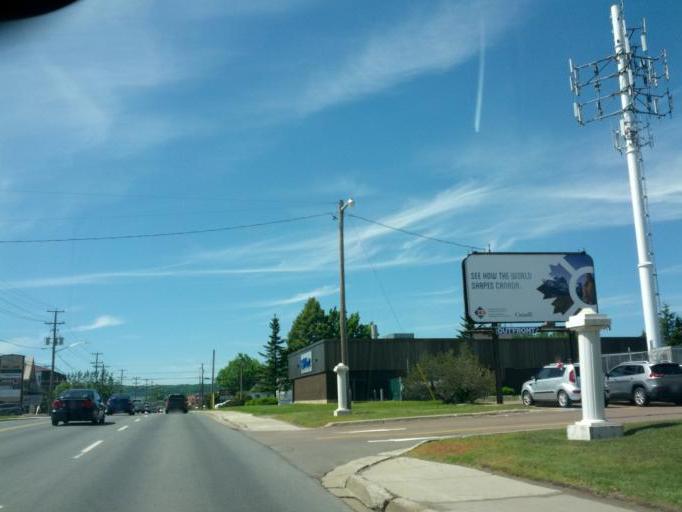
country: CA
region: New Brunswick
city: Moncton
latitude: 46.1183
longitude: -64.8417
